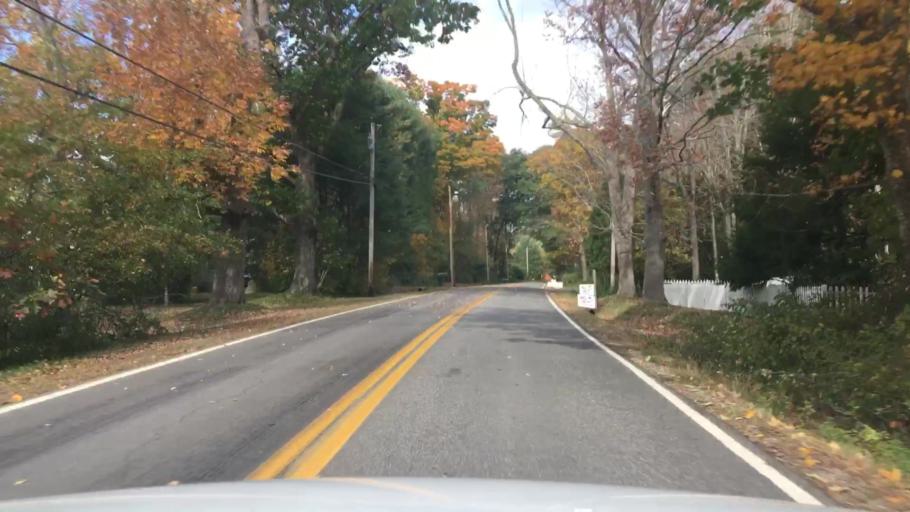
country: US
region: Maine
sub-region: Knox County
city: Hope
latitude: 44.3129
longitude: -69.1186
